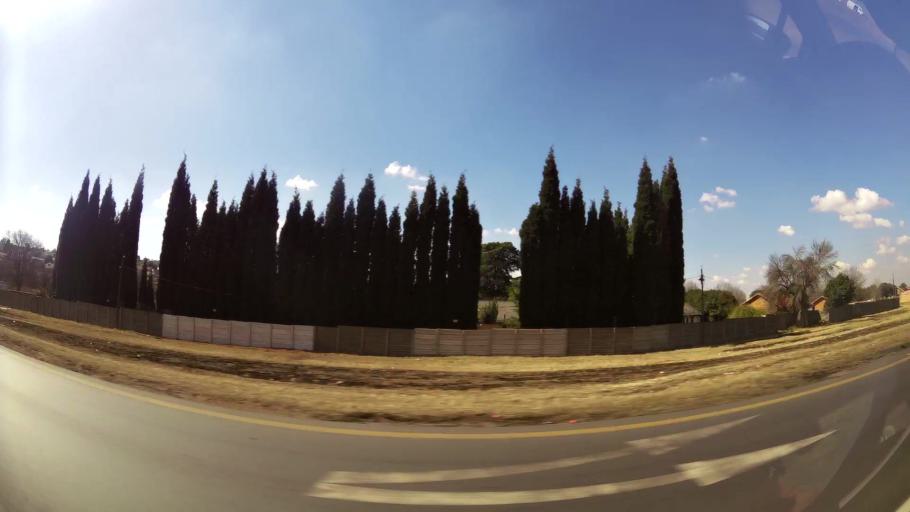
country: ZA
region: Mpumalanga
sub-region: Nkangala District Municipality
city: Witbank
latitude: -25.9337
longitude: 29.2375
